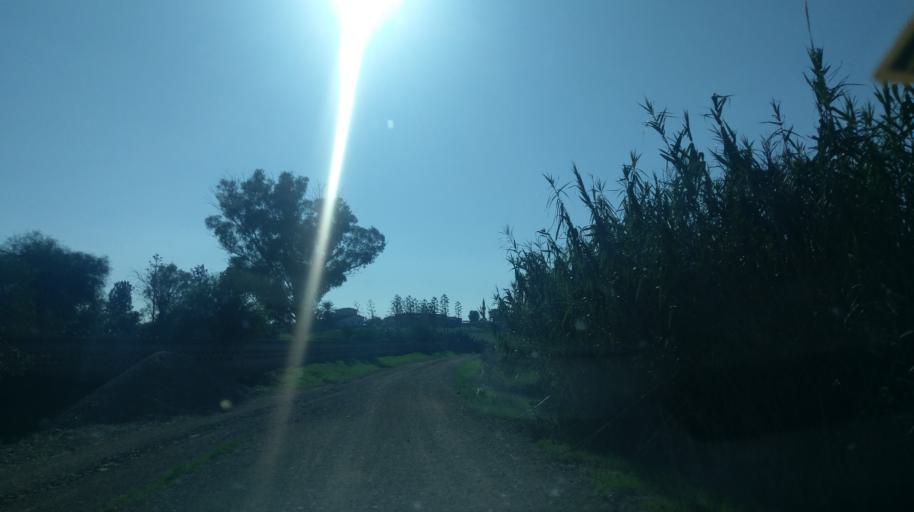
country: CY
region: Larnaka
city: Athienou
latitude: 35.1790
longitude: 33.5532
